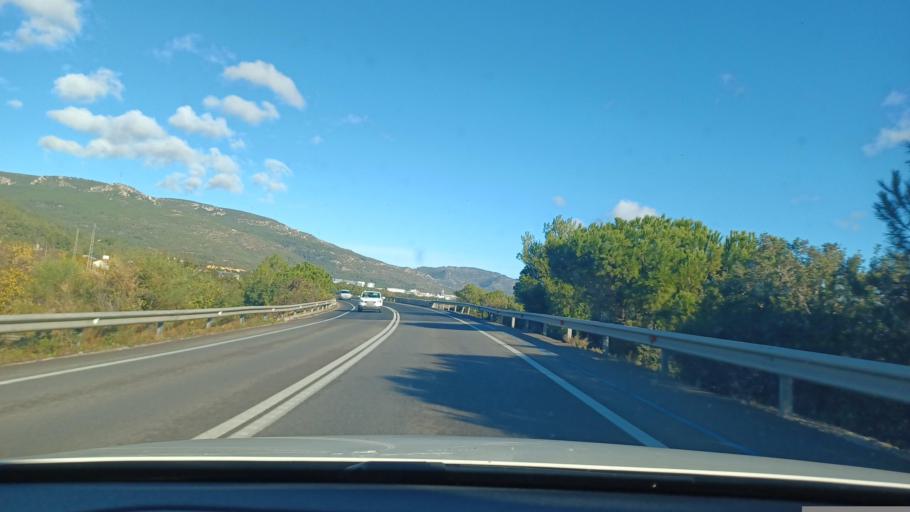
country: ES
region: Catalonia
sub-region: Provincia de Tarragona
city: Alcover
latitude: 41.2617
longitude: 1.1766
